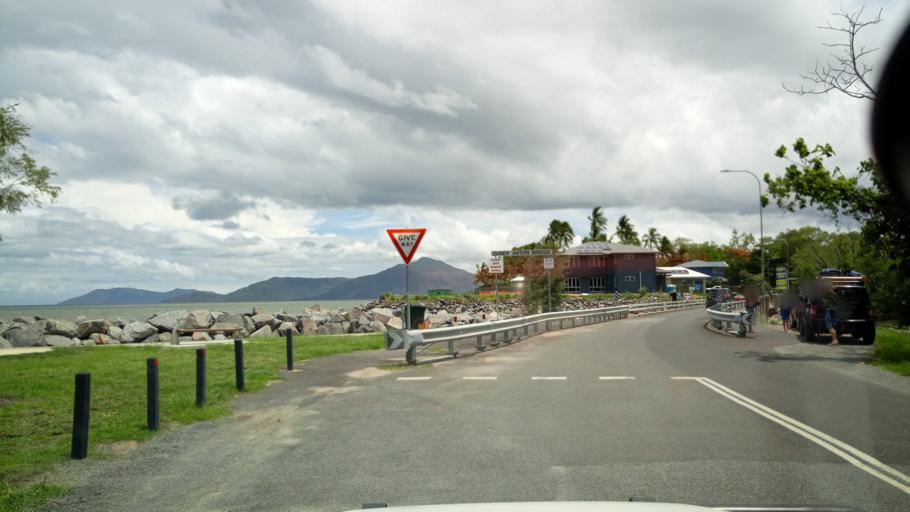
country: AU
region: Queensland
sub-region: Cairns
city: Redlynch
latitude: -16.8549
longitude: 145.7526
